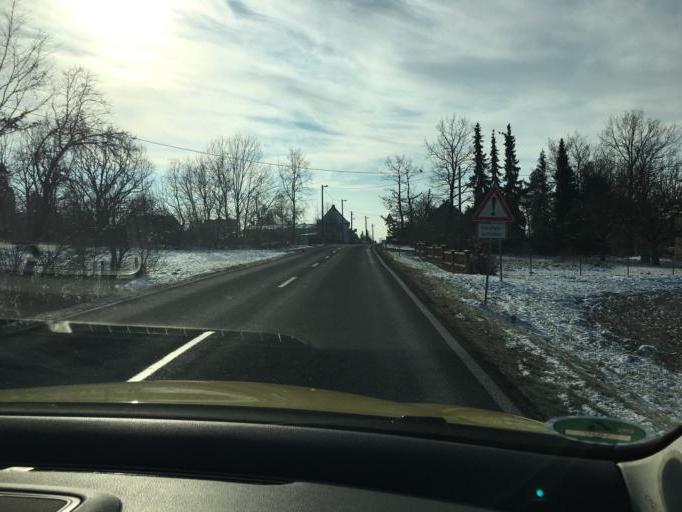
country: DE
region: Saxony
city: Otterwisch
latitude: 51.1766
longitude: 12.6219
